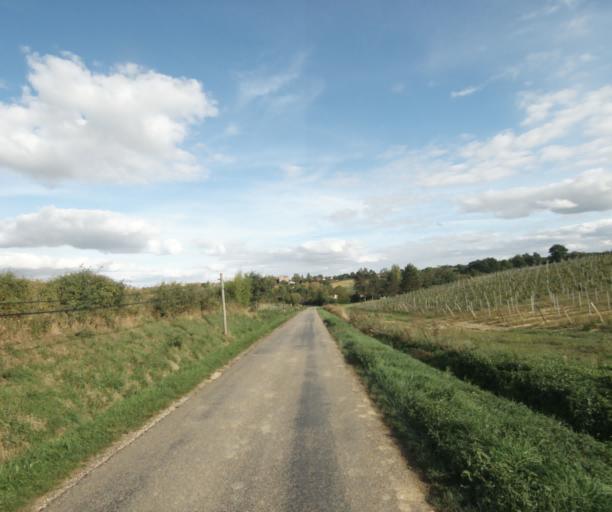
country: FR
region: Midi-Pyrenees
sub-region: Departement du Gers
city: Gondrin
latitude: 43.8858
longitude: 0.2265
